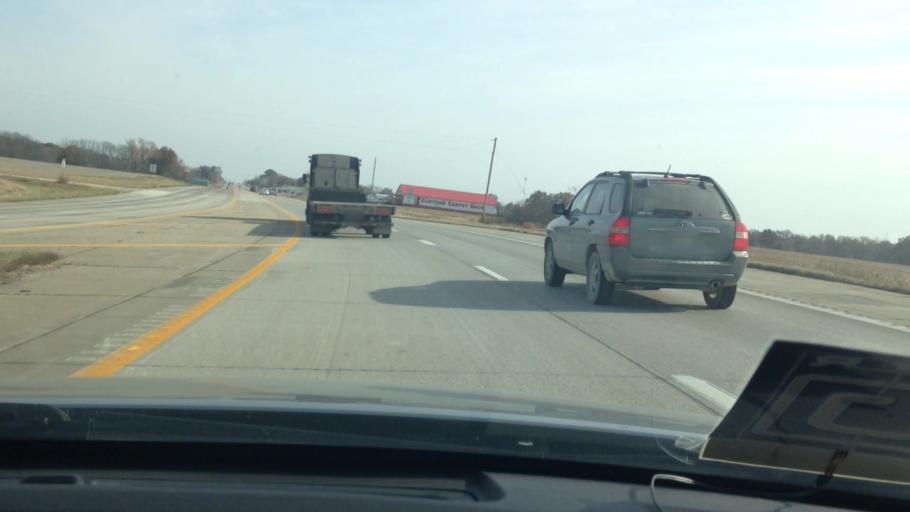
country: US
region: Missouri
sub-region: Henry County
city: Clinton
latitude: 38.3899
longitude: -93.8217
